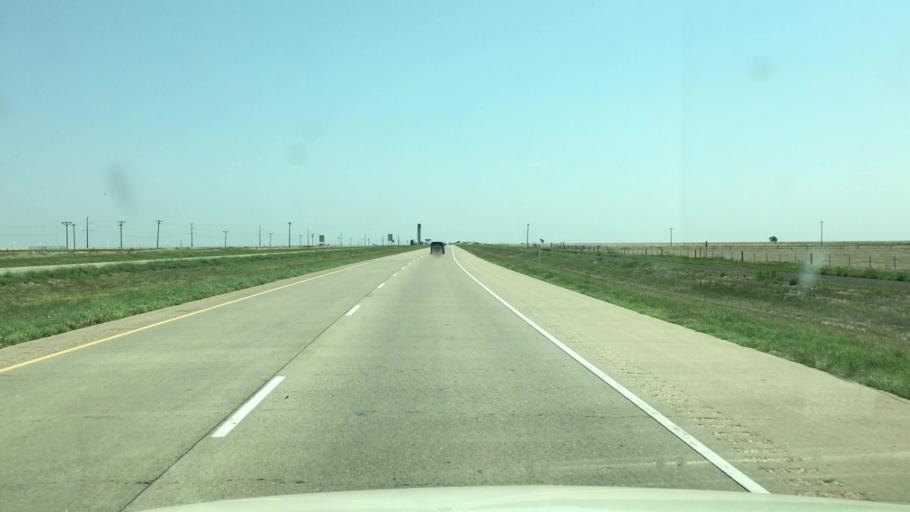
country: US
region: Texas
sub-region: Oldham County
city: Vega
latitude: 35.2728
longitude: -102.5791
